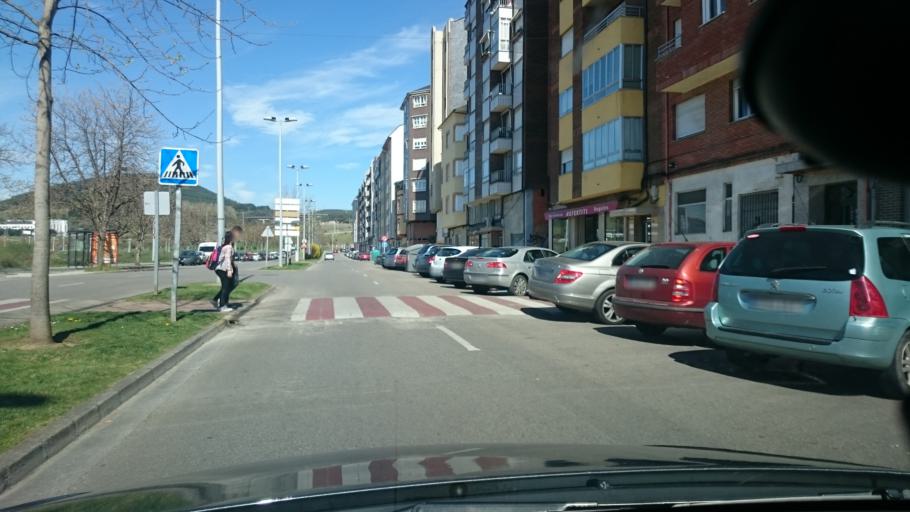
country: ES
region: Castille and Leon
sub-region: Provincia de Leon
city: Ponferrada
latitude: 42.5503
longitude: -6.5891
